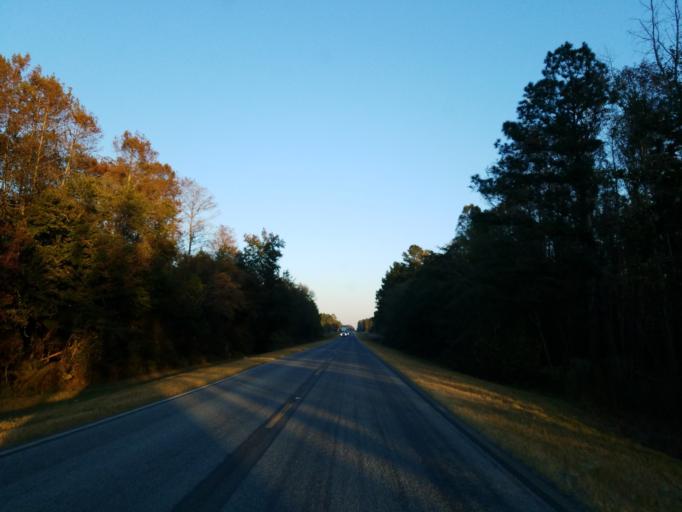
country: US
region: Georgia
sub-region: Ben Hill County
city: Fitzgerald
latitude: 31.7210
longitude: -83.4462
